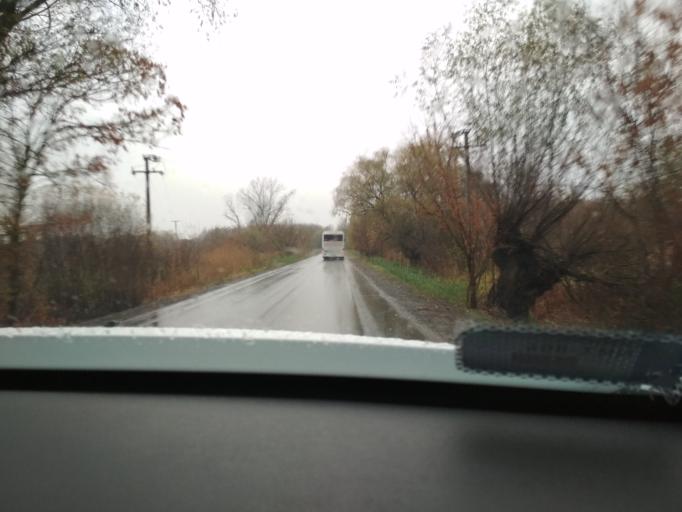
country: HU
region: Csongrad
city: Opusztaszer
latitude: 46.4403
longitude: 20.1286
